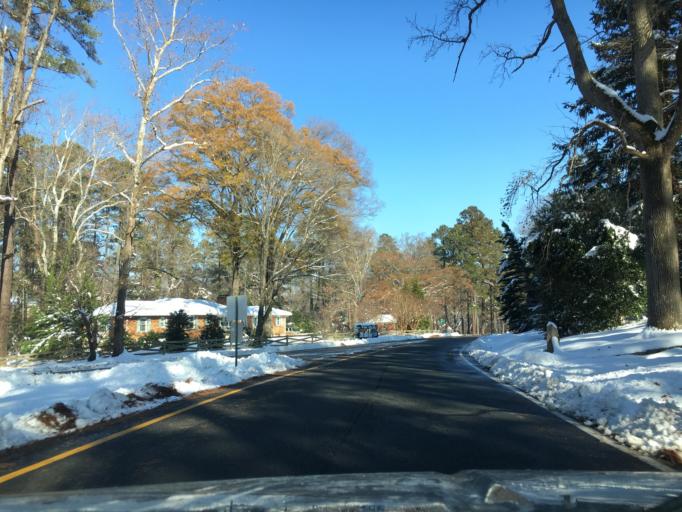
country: US
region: Virginia
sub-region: Henrico County
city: Tuckahoe
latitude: 37.5819
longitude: -77.5499
